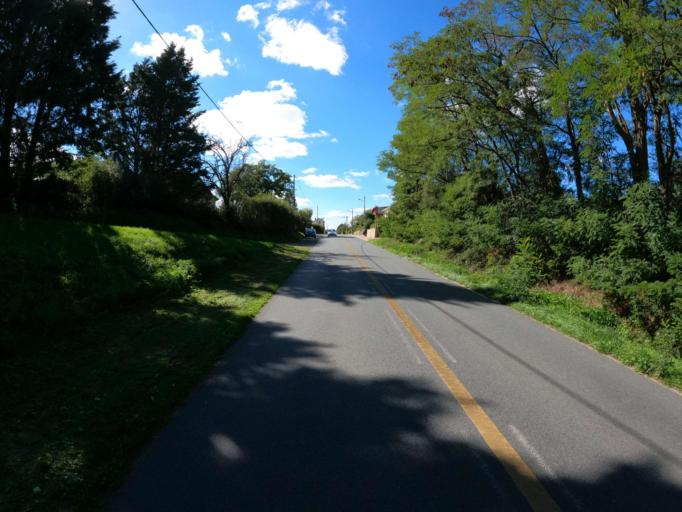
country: FR
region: Auvergne
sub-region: Departement de l'Allier
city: Doyet
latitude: 46.3965
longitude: 2.8635
